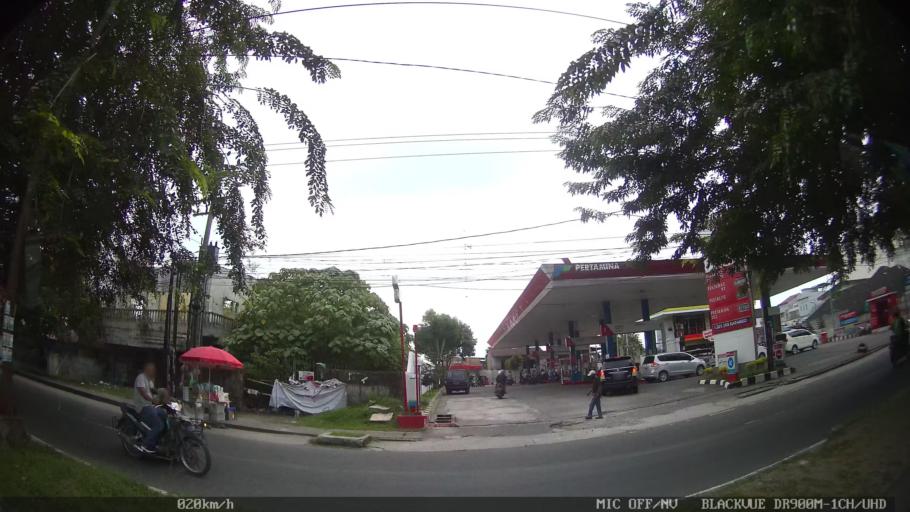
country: ID
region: North Sumatra
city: Medan
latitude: 3.5596
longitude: 98.6889
